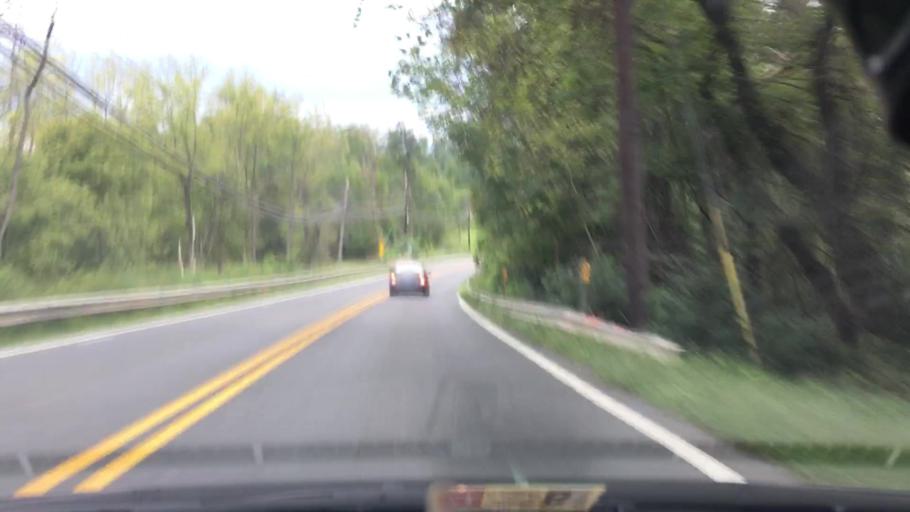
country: US
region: Maryland
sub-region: Montgomery County
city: Clarksburg
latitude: 39.2211
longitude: -77.2591
